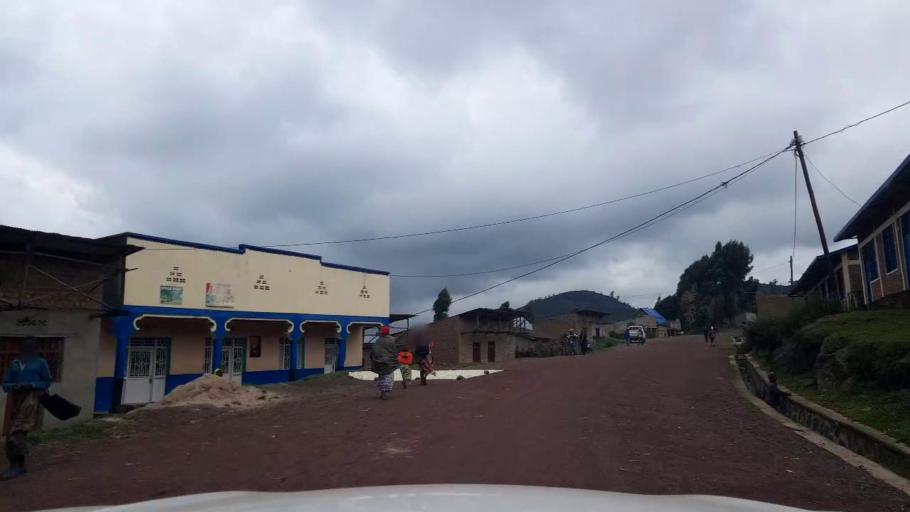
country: RW
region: Northern Province
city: Musanze
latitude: -1.5823
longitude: 29.4749
